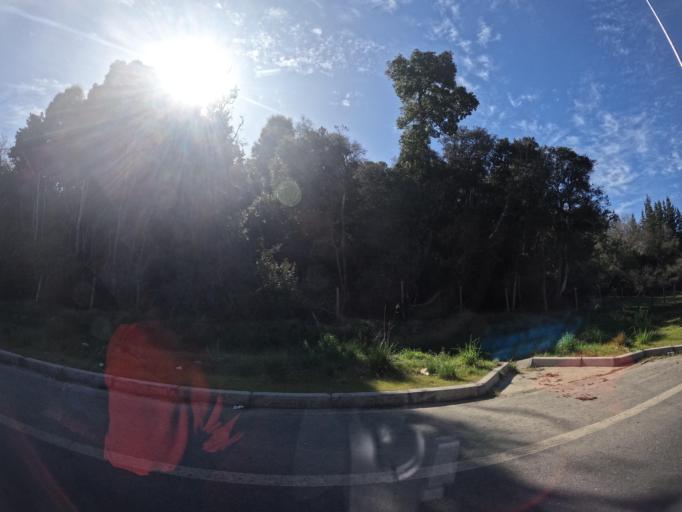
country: CL
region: Biobio
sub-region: Provincia de Biobio
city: Yumbel
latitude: -36.9612
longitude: -72.7217
